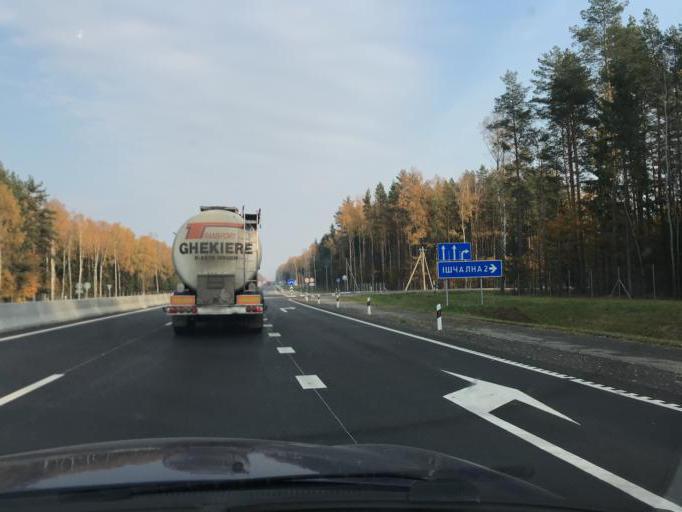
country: BY
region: Grodnenskaya
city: Shchuchin
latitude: 53.6824
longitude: 24.8499
